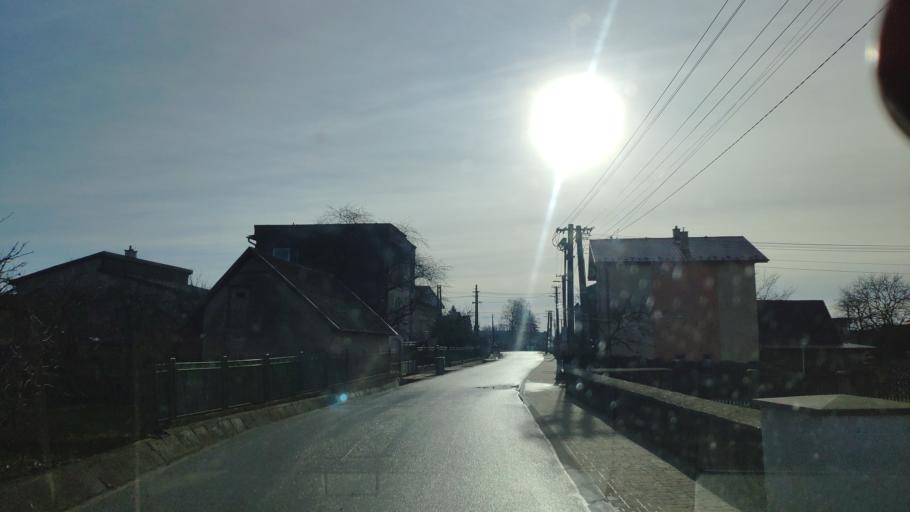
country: SK
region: Kosicky
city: Kosice
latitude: 48.6941
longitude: 21.3433
